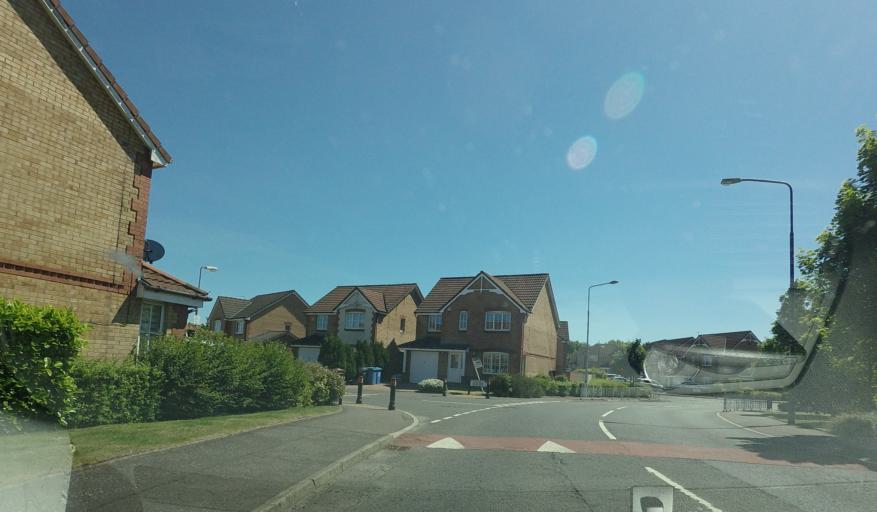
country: GB
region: Scotland
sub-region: West Lothian
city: Broxburn
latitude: 55.9308
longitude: -3.4809
